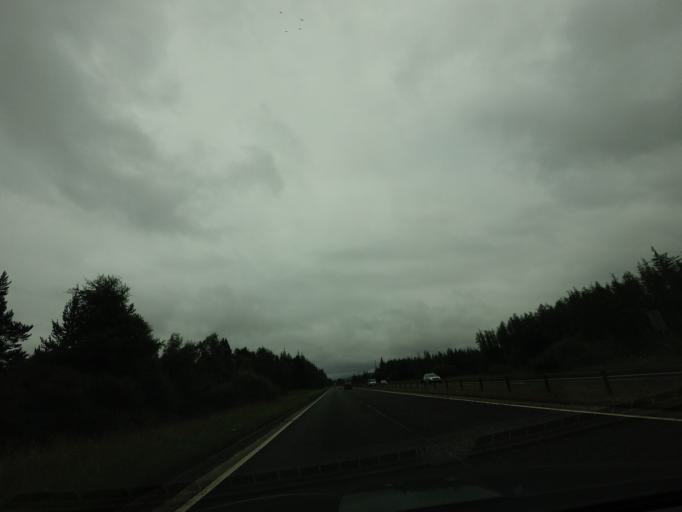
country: GB
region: Scotland
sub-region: Highland
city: Inverness
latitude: 57.4432
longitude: -4.1477
